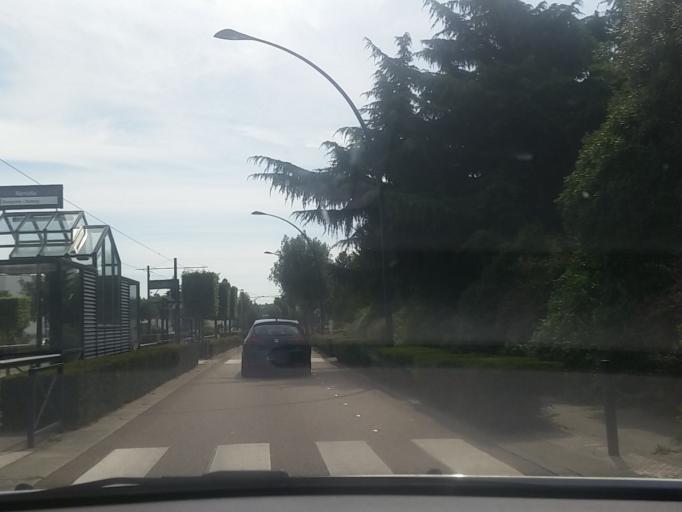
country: FR
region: Pays de la Loire
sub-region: Departement de la Loire-Atlantique
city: Saint-Herblain
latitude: 47.2176
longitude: -1.6140
